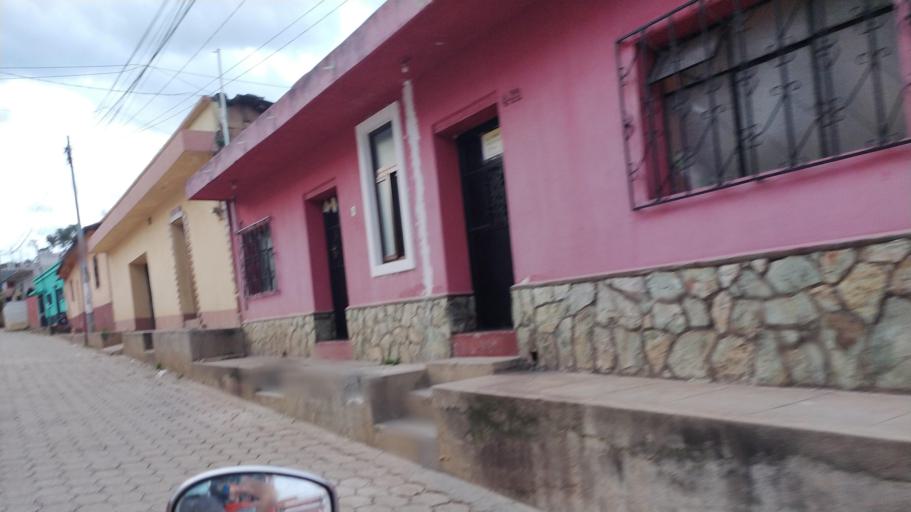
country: GT
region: Quetzaltenango
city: Salcaja
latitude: 14.8825
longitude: -91.4602
